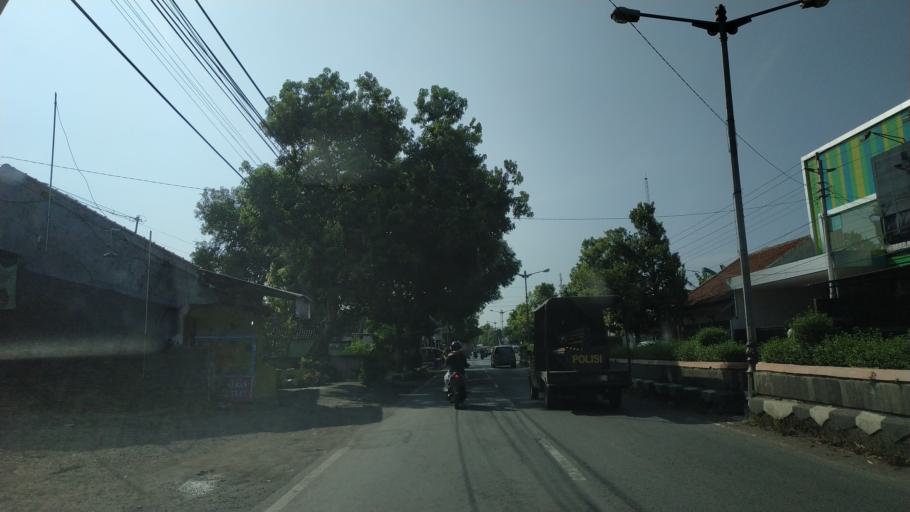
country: ID
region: Central Java
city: Petarukan
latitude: -6.8922
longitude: 109.4018
